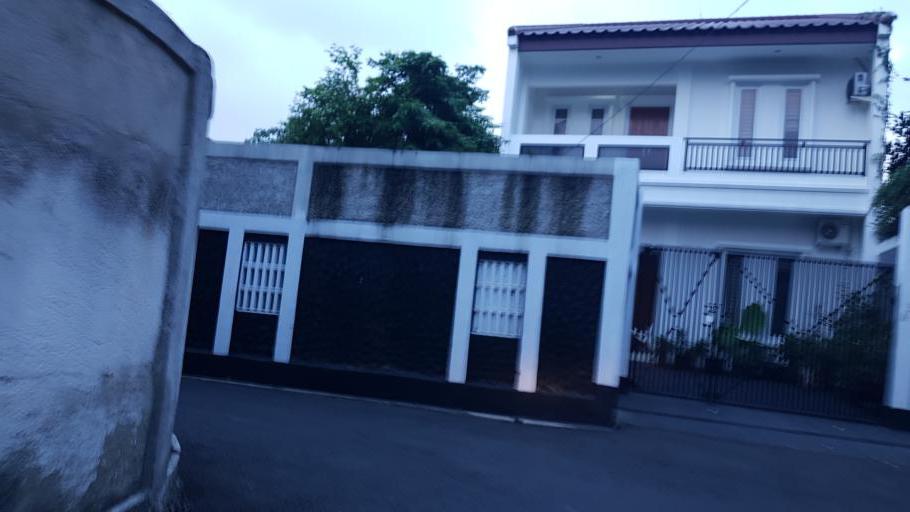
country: ID
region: West Java
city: Pamulang
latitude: -6.2973
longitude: 106.7897
